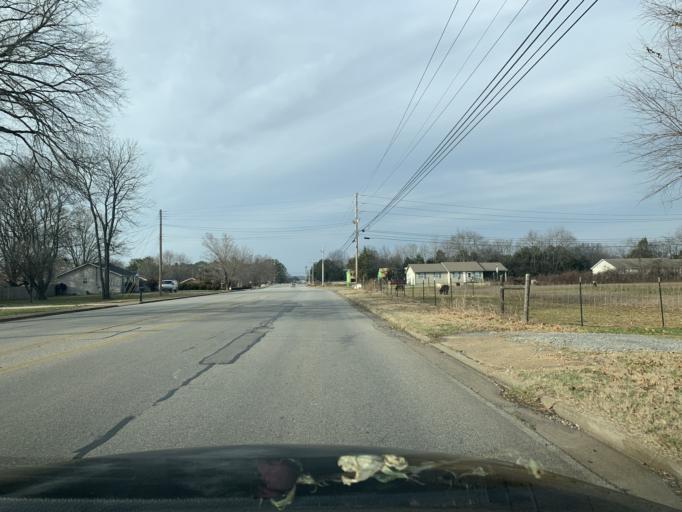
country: US
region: Tennessee
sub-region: Rutherford County
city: Smyrna
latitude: 35.9422
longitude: -86.5014
